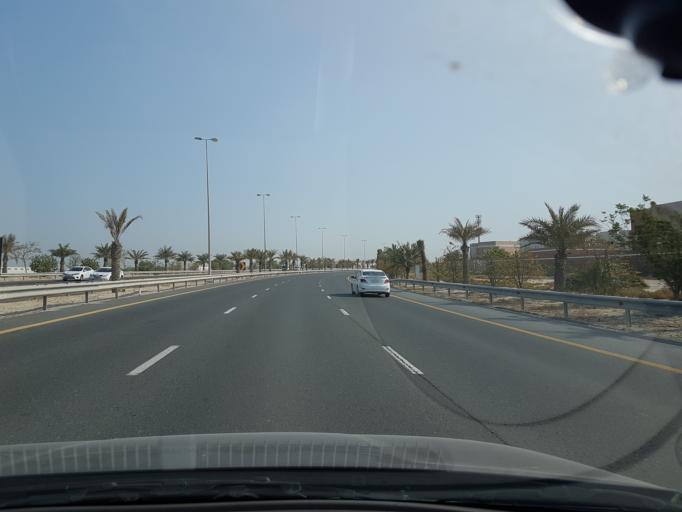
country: BH
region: Central Governorate
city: Madinat Hamad
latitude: 26.0909
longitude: 50.5393
